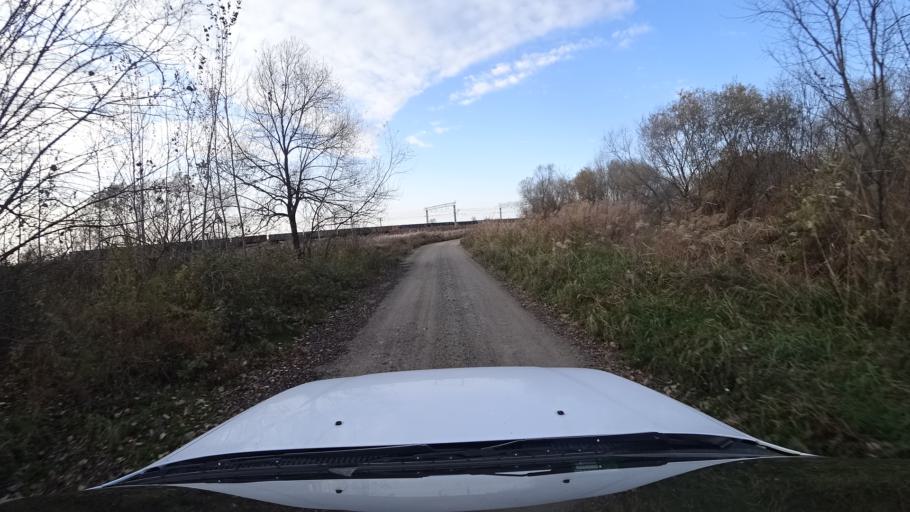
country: RU
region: Primorskiy
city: Lazo
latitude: 45.8177
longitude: 133.6104
